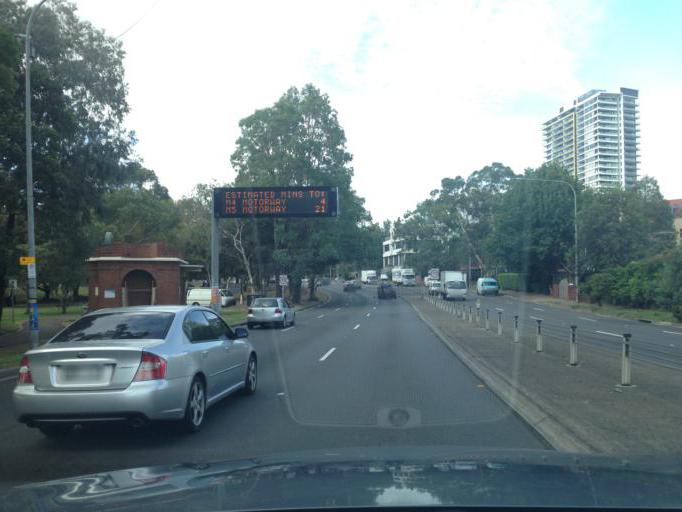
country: AU
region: New South Wales
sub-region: Canada Bay
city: Rhodes
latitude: -33.8292
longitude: 151.0888
